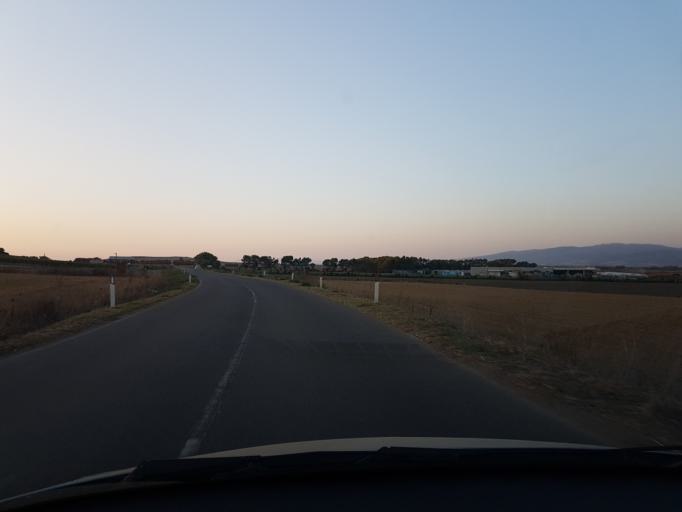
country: IT
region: Sardinia
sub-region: Provincia di Oristano
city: Cabras
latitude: 39.9621
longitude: 8.4540
